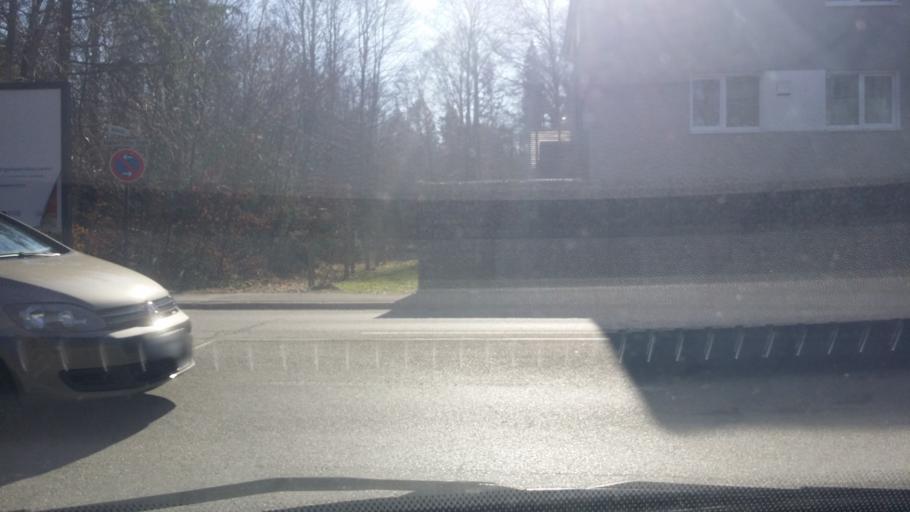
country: DE
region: Bavaria
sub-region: Upper Bavaria
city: Geretsried
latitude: 47.8629
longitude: 11.4806
